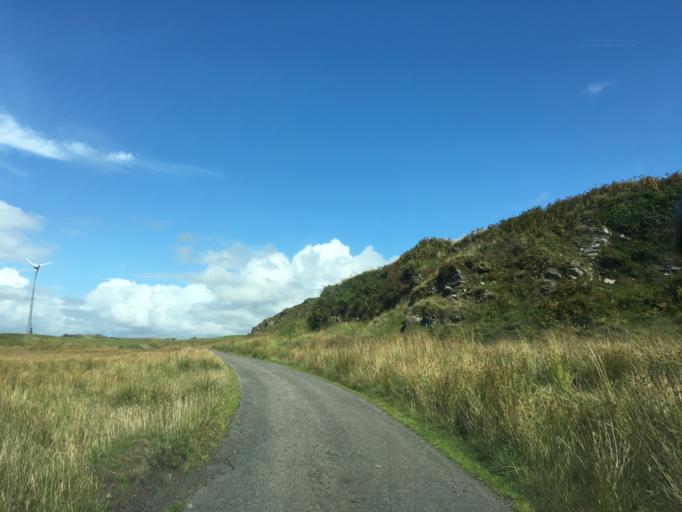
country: GB
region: Scotland
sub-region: Argyll and Bute
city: Isle Of Mull
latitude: 56.2194
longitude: -5.6496
